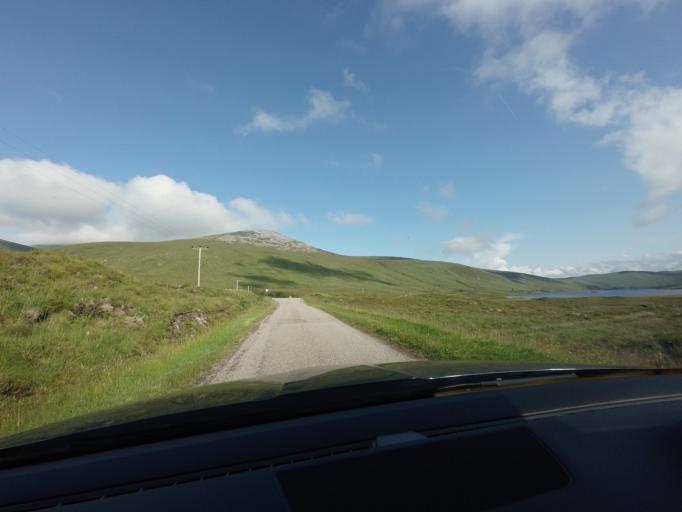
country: GB
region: Scotland
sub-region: Highland
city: Ullapool
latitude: 58.2554
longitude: -4.7595
